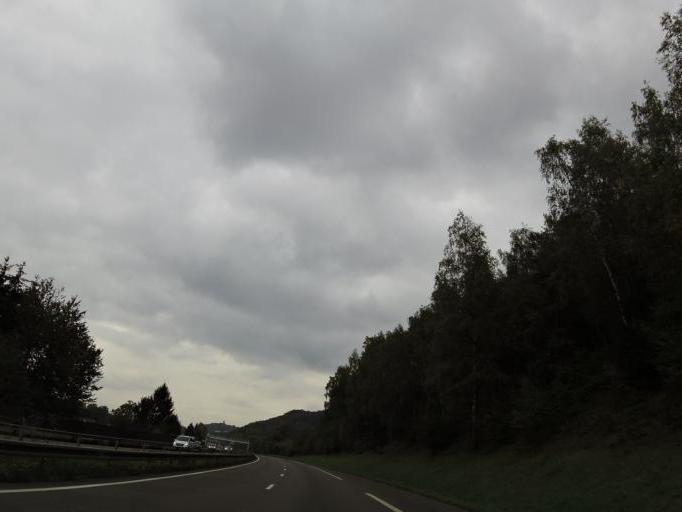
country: FR
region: Lorraine
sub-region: Departement de la Moselle
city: Morsbach
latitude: 49.1654
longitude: 6.8736
